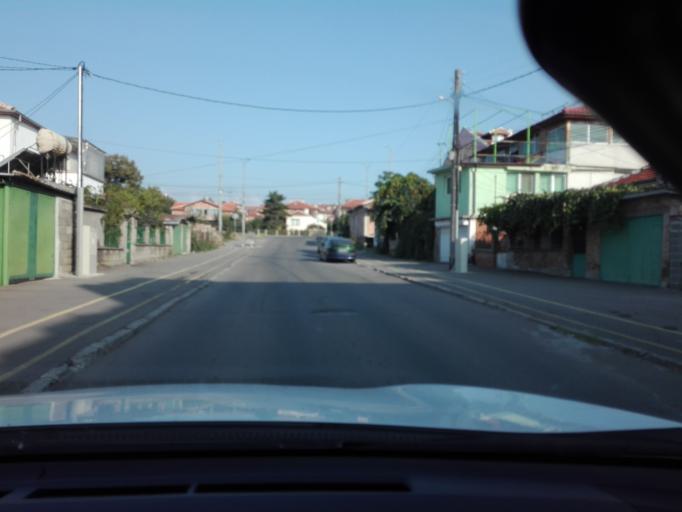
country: BG
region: Burgas
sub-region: Obshtina Burgas
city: Burgas
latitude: 42.4583
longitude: 27.4074
